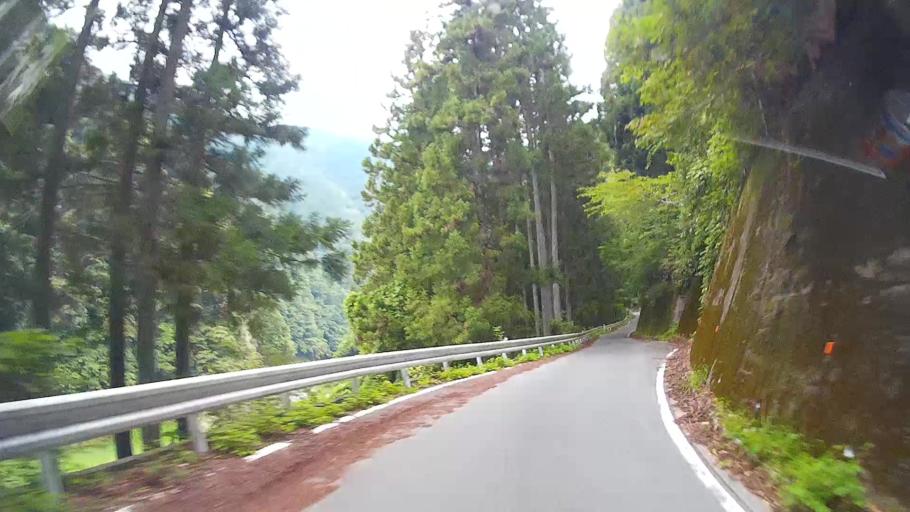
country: JP
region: Saitama
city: Chichibu
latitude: 35.9423
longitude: 138.8845
